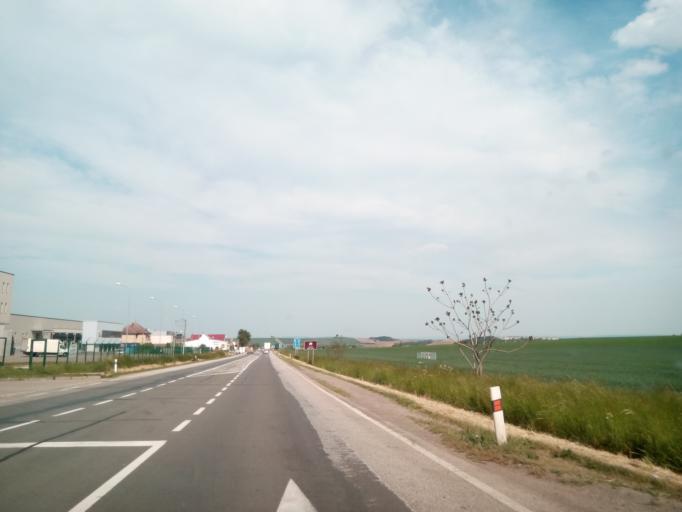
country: CZ
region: South Moravian
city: Podoli
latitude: 49.1823
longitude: 16.6957
